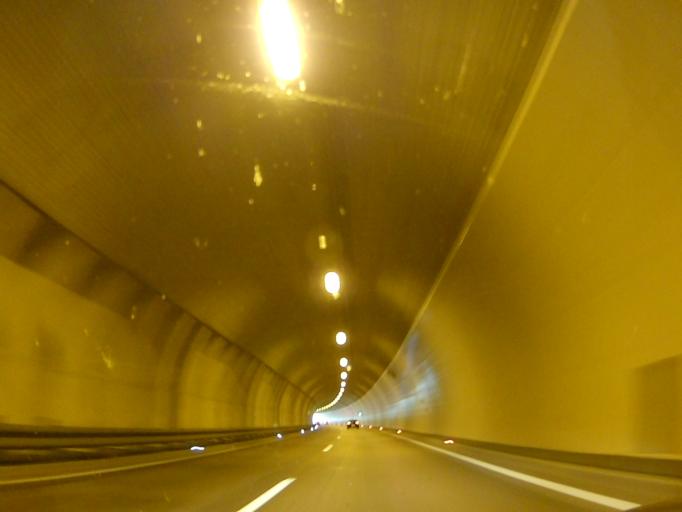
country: AT
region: Tyrol
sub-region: Politischer Bezirk Imst
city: Silz
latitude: 47.2706
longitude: 10.9117
